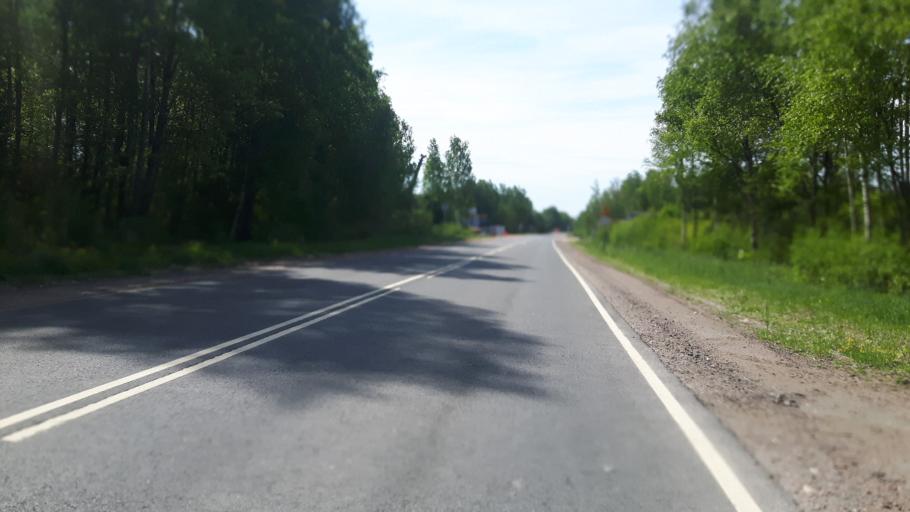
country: RU
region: Leningrad
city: Vistino
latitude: 59.6842
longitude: 28.4589
